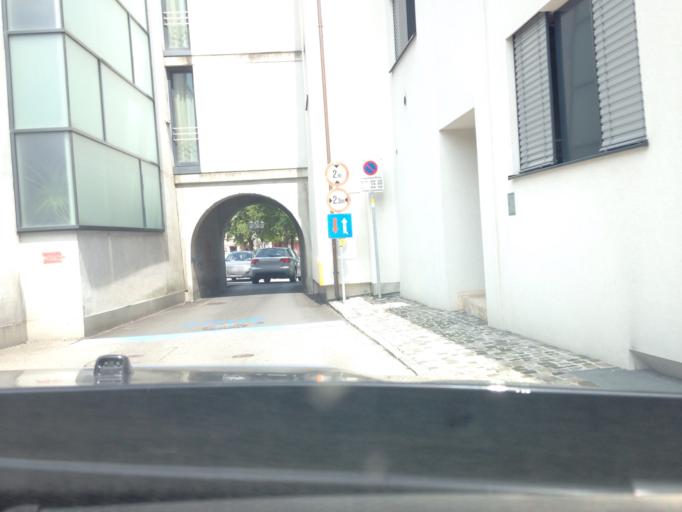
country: AT
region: Vorarlberg
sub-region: Politischer Bezirk Dornbirn
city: Hohenems
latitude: 47.3619
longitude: 9.6896
